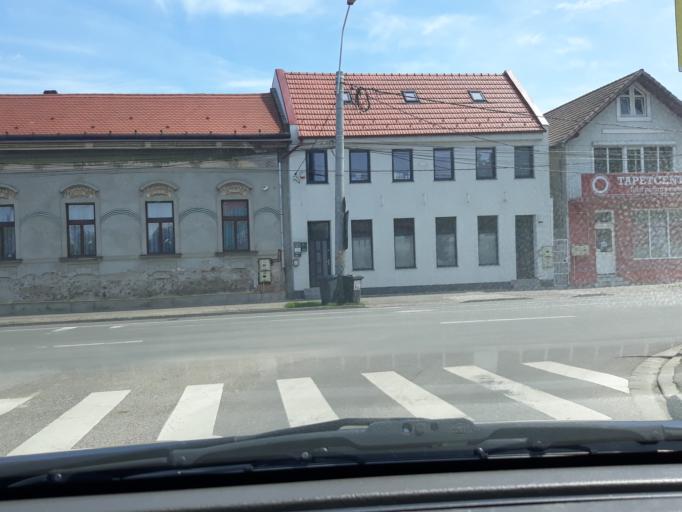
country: RO
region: Bihor
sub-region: Comuna Biharea
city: Oradea
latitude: 47.0520
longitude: 21.9190
